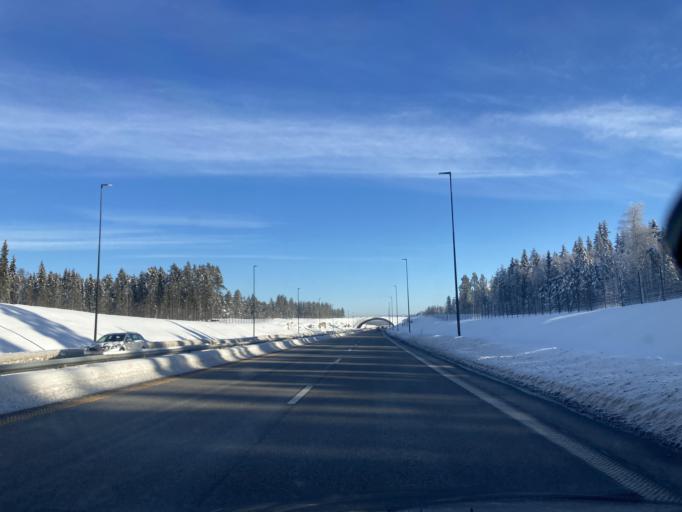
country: NO
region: Hedmark
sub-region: Loten
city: Loten
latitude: 60.8580
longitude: 11.4048
